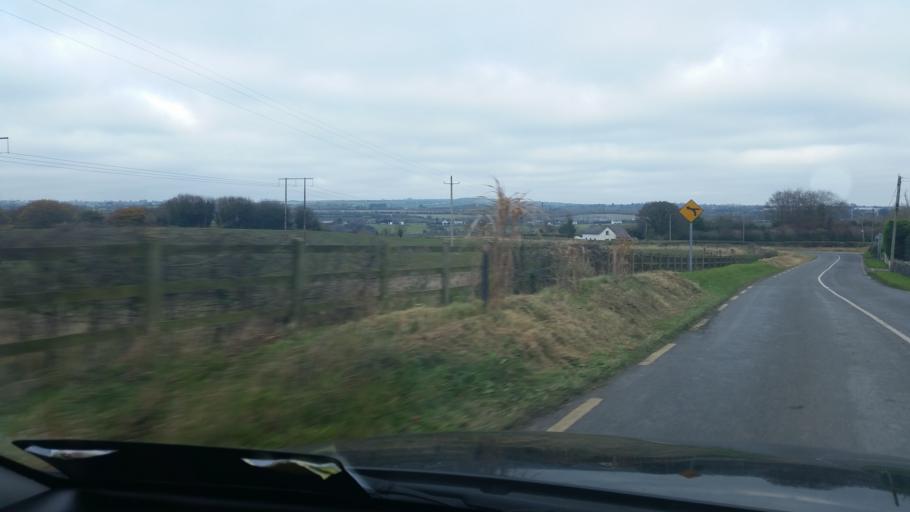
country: IE
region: Leinster
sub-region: Lu
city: Tullyallen
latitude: 53.7138
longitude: -6.4119
